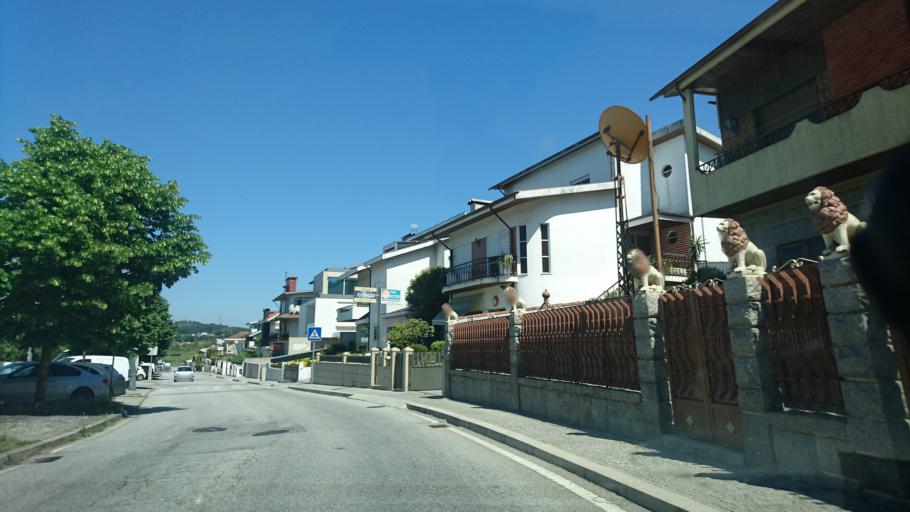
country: PT
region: Porto
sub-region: Paredes
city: Baltar
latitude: 41.1671
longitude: -8.3495
